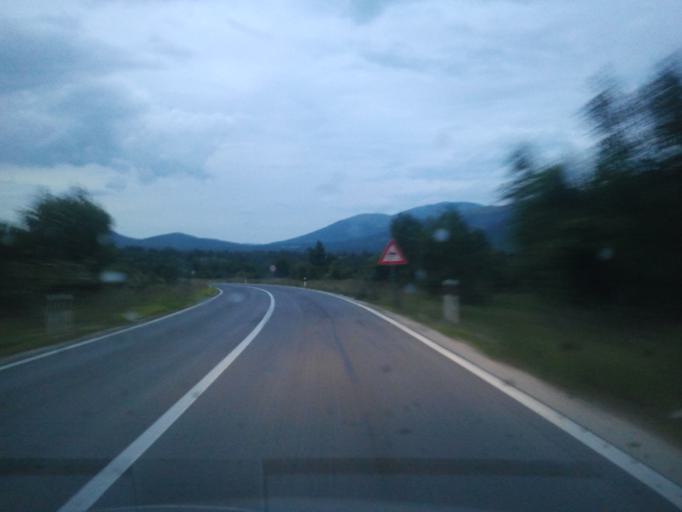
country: HR
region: Zadarska
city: Gracac
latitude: 44.4177
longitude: 15.8876
